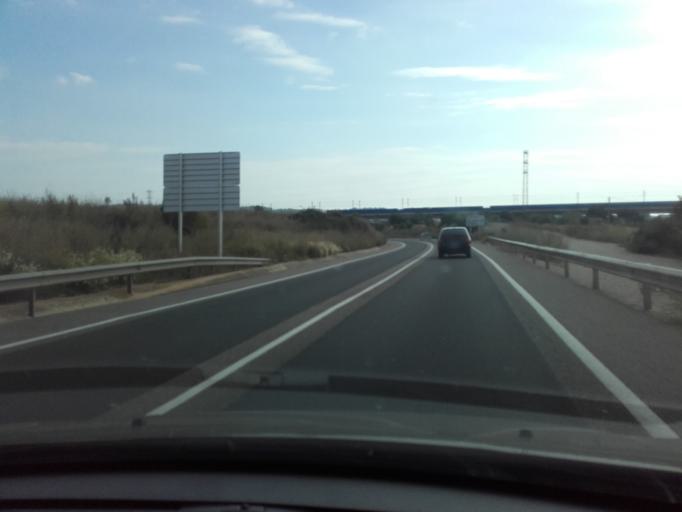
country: ES
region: Catalonia
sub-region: Provincia de Tarragona
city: El Vendrell
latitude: 41.2339
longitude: 1.5334
